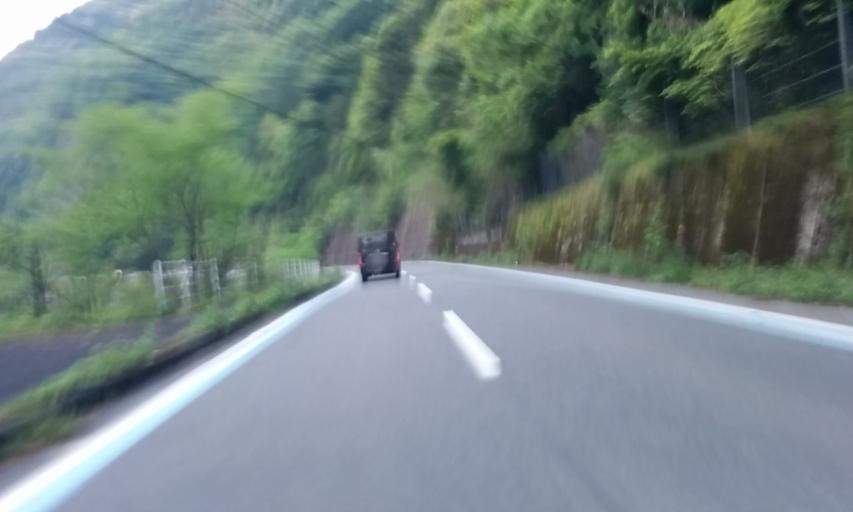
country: JP
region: Ehime
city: Saijo
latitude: 33.8558
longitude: 133.1975
